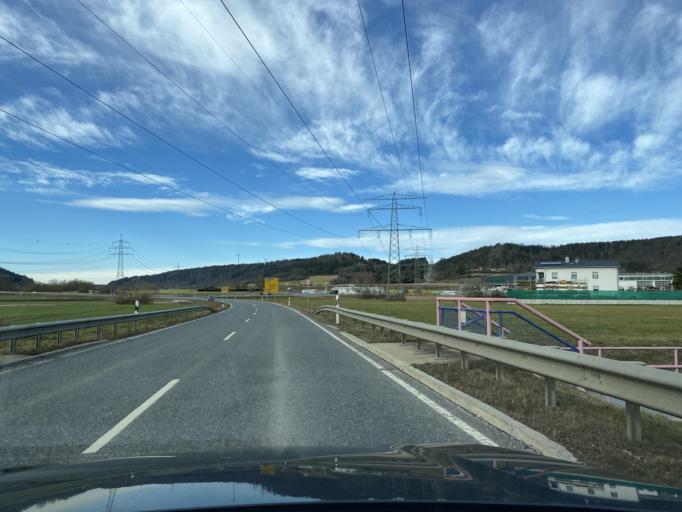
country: DE
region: Bavaria
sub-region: Upper Palatinate
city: Dietfurt
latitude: 49.0309
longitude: 11.5774
